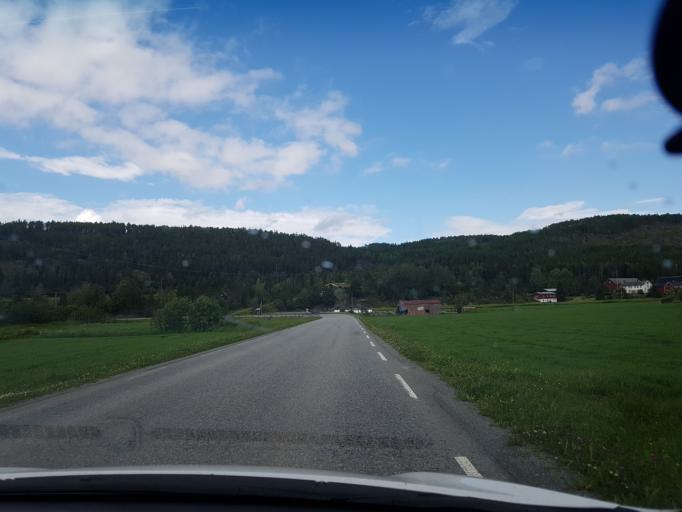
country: NO
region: Nord-Trondelag
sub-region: Stjordal
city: Stjordalshalsen
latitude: 63.6115
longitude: 10.9363
